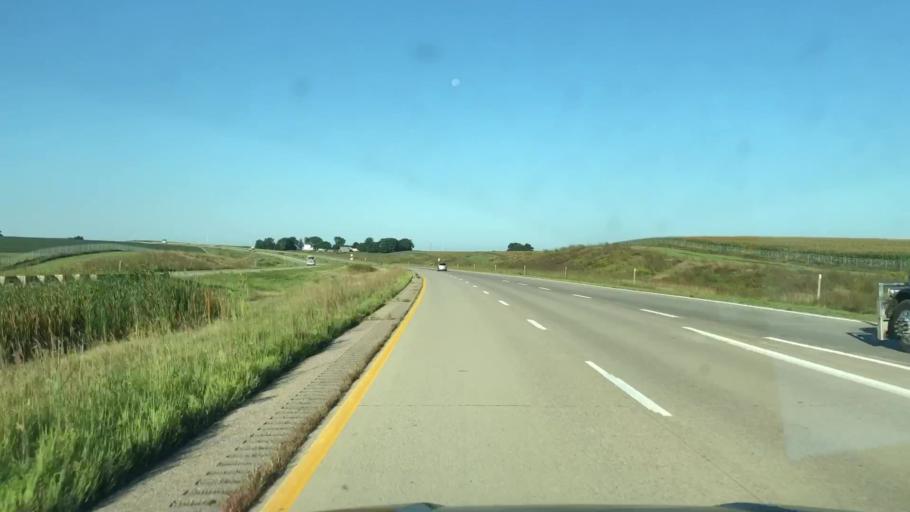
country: US
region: Iowa
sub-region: Plymouth County
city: Le Mars
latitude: 42.8175
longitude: -96.1811
